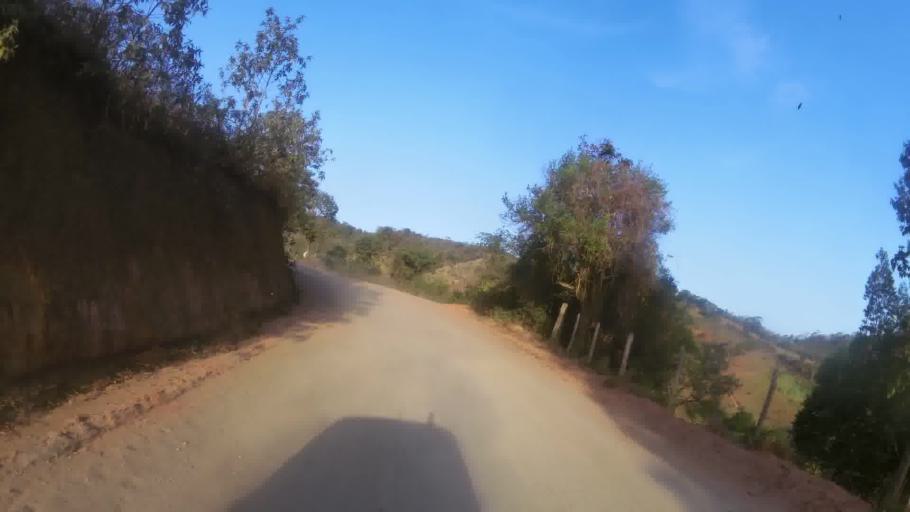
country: BR
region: Espirito Santo
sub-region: Iconha
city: Iconha
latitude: -20.8981
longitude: -40.8098
